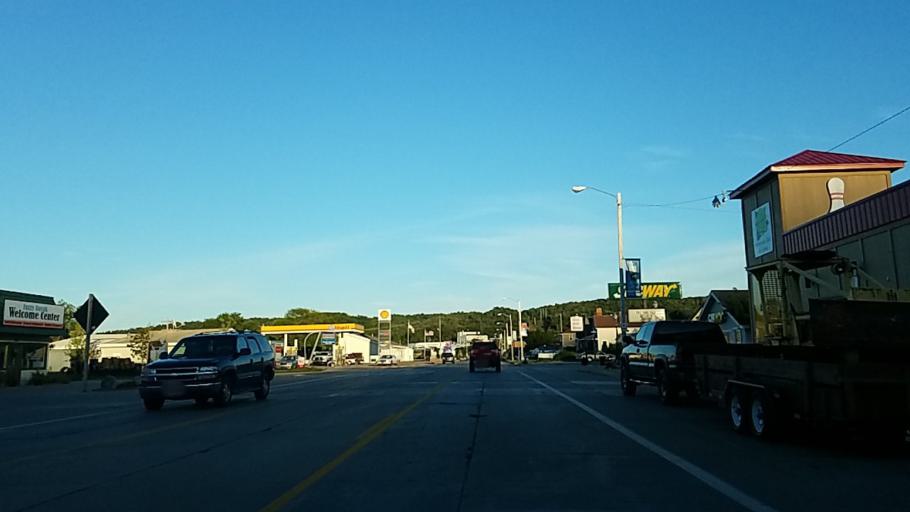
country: US
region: Michigan
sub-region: Alger County
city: Munising
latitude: 46.4112
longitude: -86.6541
